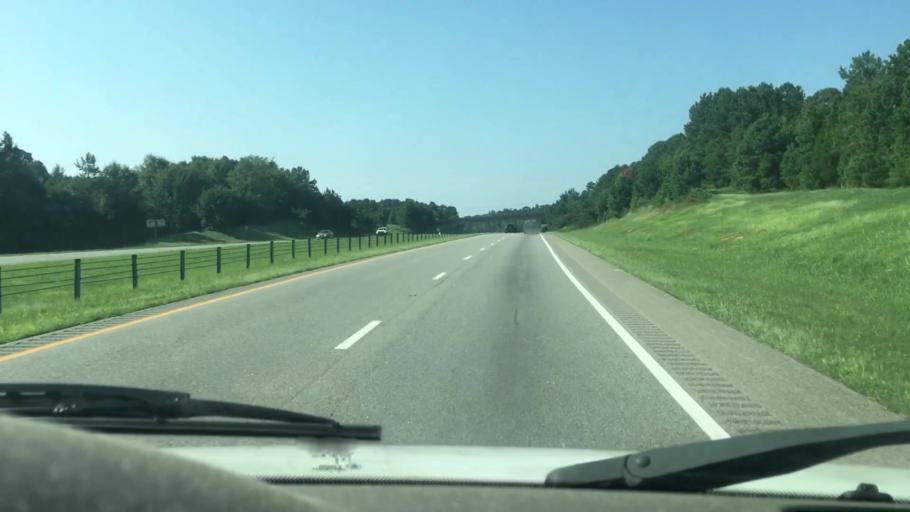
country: US
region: North Carolina
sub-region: Lincoln County
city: Lowesville
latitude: 35.3917
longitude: -80.9988
